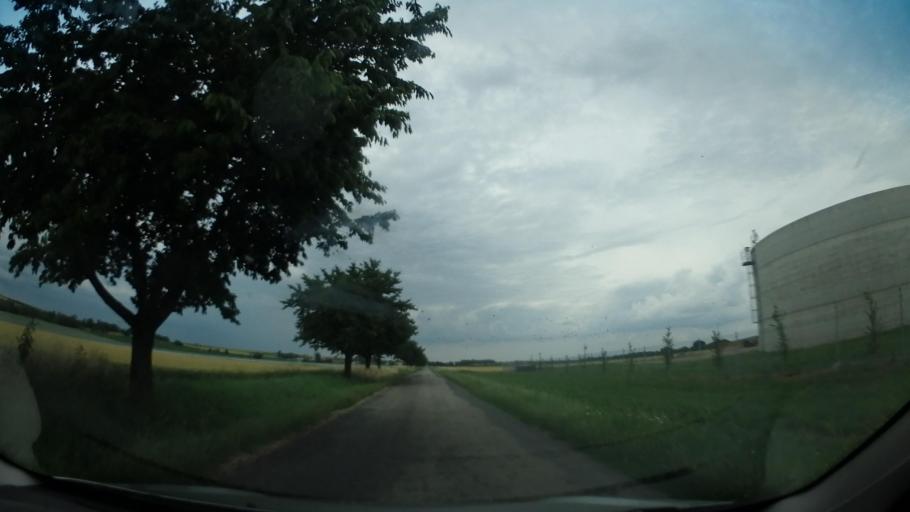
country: CZ
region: South Moravian
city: Ivanovice na Hane
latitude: 49.3207
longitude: 17.1255
